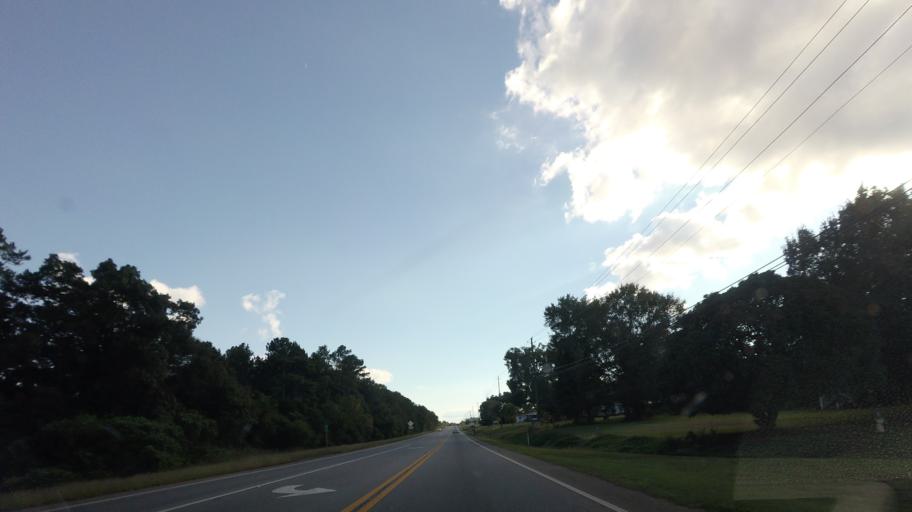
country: US
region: Georgia
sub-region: Upson County
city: Thomaston
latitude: 32.9182
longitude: -84.2908
